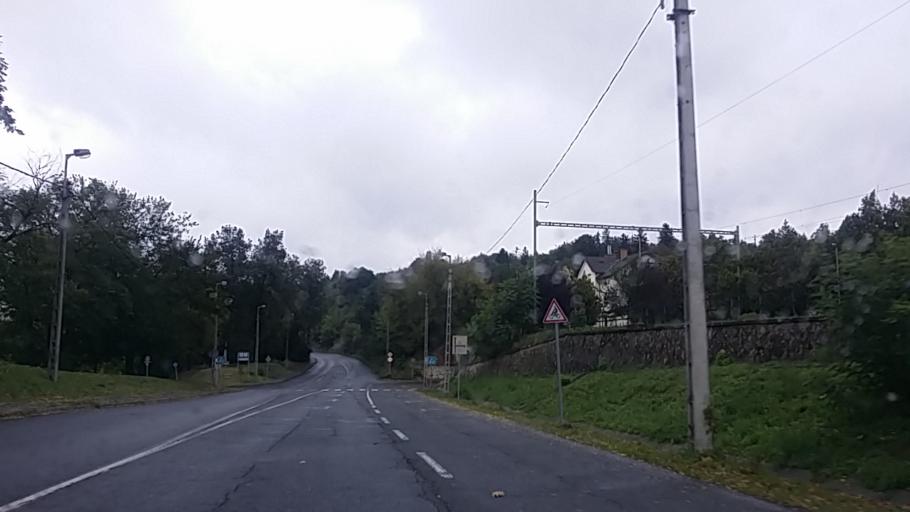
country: HU
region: Komarom-Esztergom
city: Pilismarot
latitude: 47.7997
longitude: 18.9089
